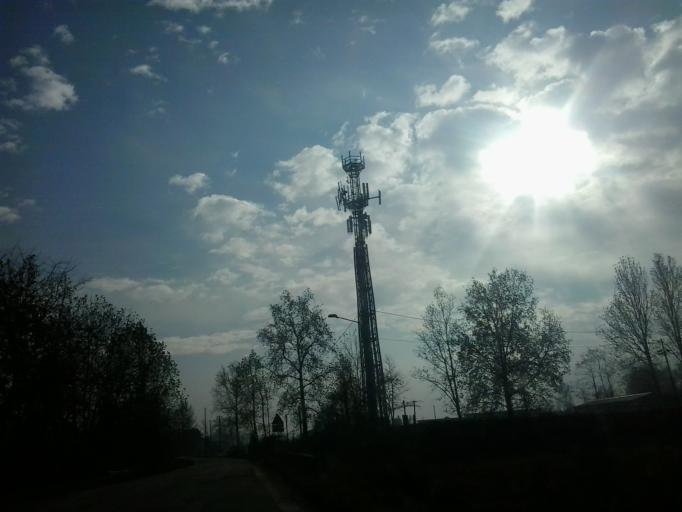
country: IT
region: Lombardy
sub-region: Provincia di Brescia
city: Azzano Mella
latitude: 45.4500
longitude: 10.1171
